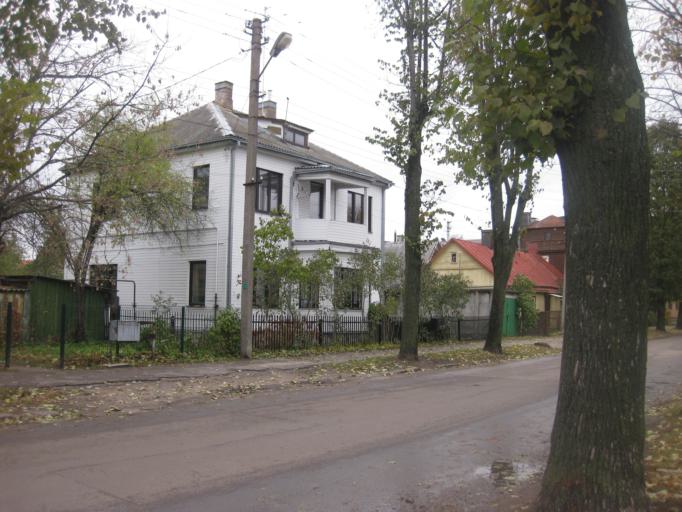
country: LT
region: Kauno apskritis
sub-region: Kaunas
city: Eiguliai
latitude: 54.9088
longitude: 23.9244
